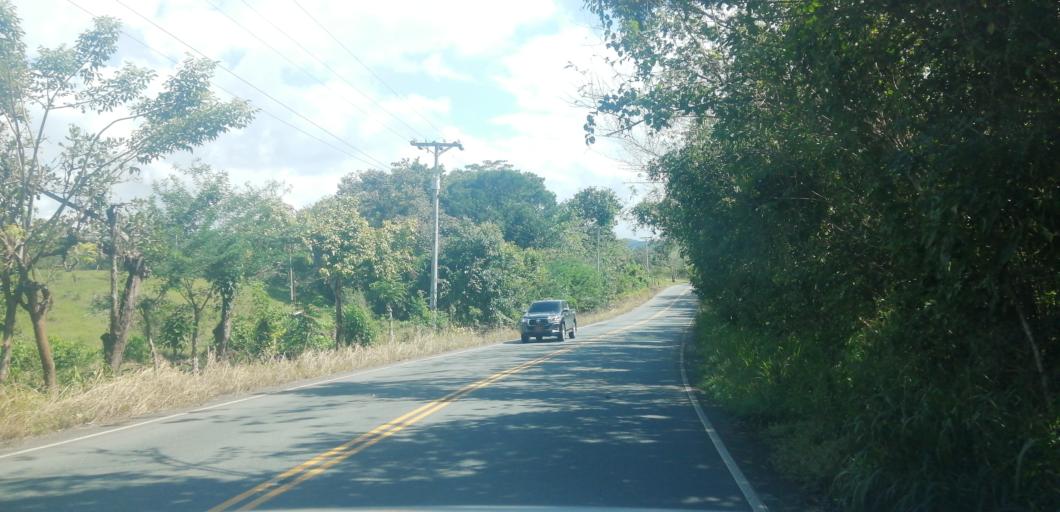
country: PA
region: Panama
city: Canita
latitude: 9.2211
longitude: -78.9247
